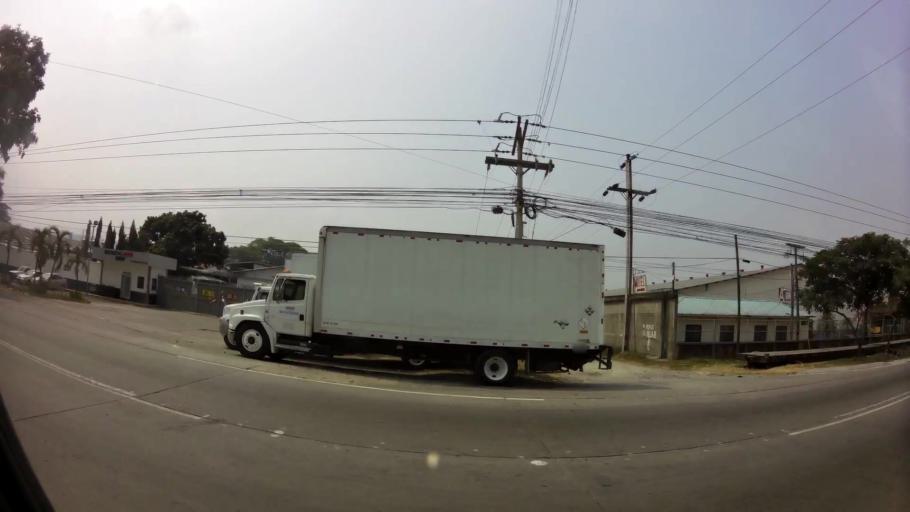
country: HN
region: Cortes
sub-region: San Pedro Sula
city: Pena Blanca
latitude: 15.5526
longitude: -87.9997
